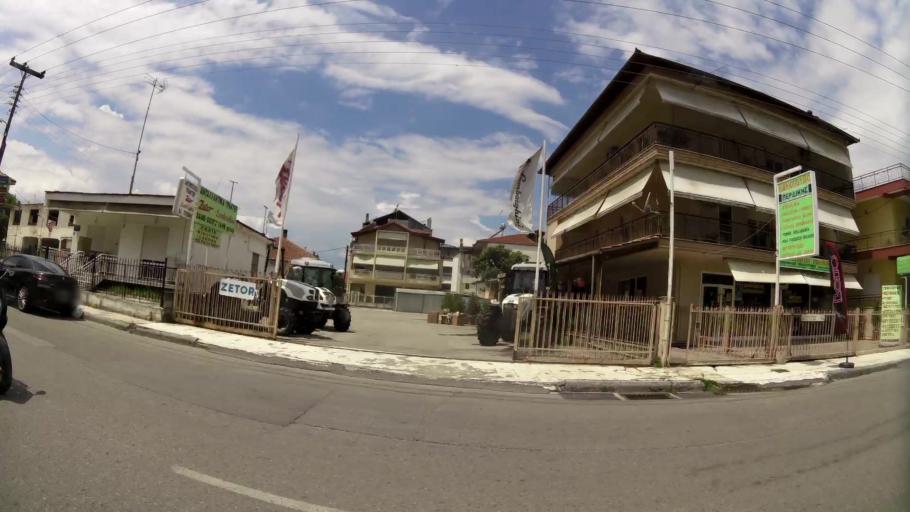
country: GR
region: Central Macedonia
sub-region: Nomos Pierias
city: Katerini
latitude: 40.2635
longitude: 22.5087
